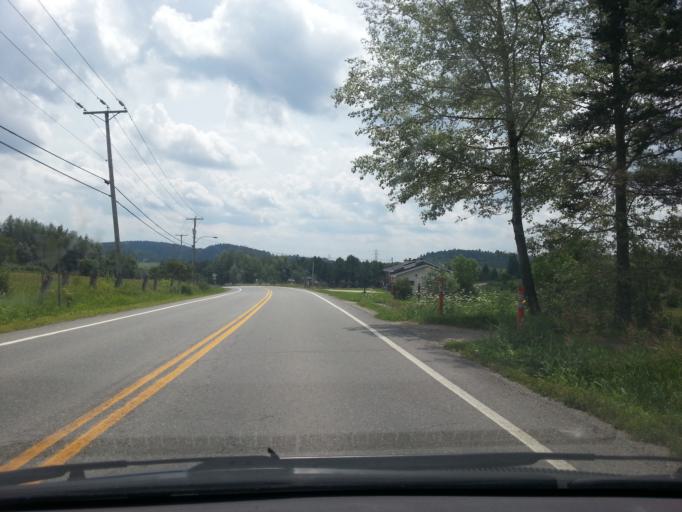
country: CA
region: Quebec
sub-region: Outaouais
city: Wakefield
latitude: 45.6222
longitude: -75.8005
